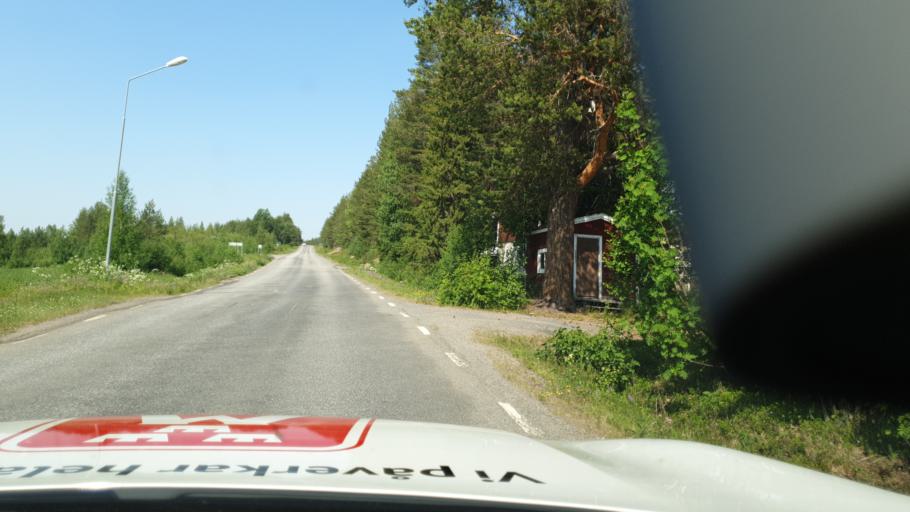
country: SE
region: Vaesterbotten
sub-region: Skelleftea Kommun
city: Langsele
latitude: 64.9568
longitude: 19.9106
